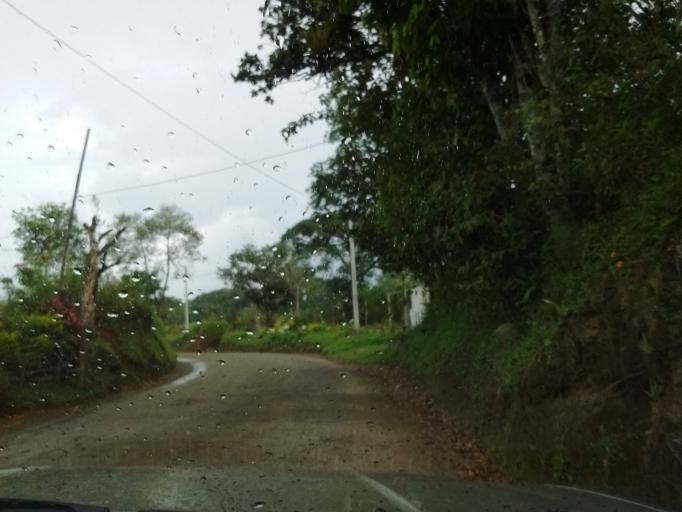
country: CO
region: Cauca
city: Popayan
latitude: 2.5208
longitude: -76.5925
